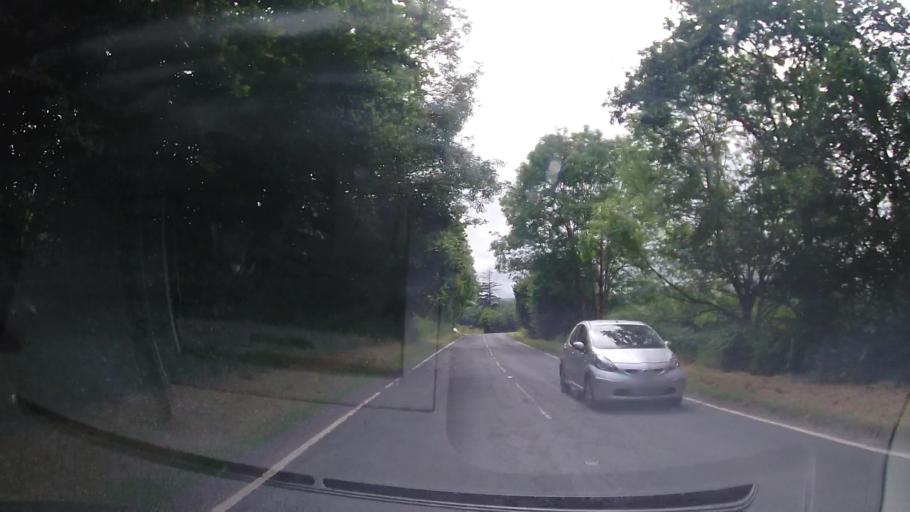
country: GB
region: Wales
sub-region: Denbighshire
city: Corwen
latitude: 52.9690
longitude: -3.3938
